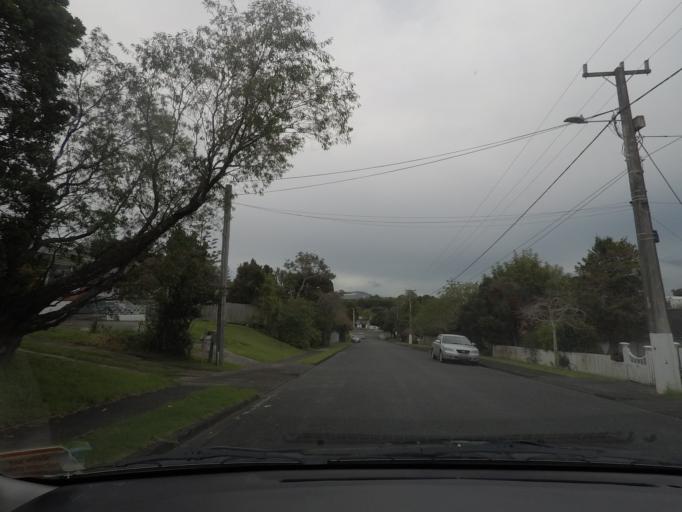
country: NZ
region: Auckland
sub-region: Auckland
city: Rosebank
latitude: -36.8577
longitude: 174.6412
